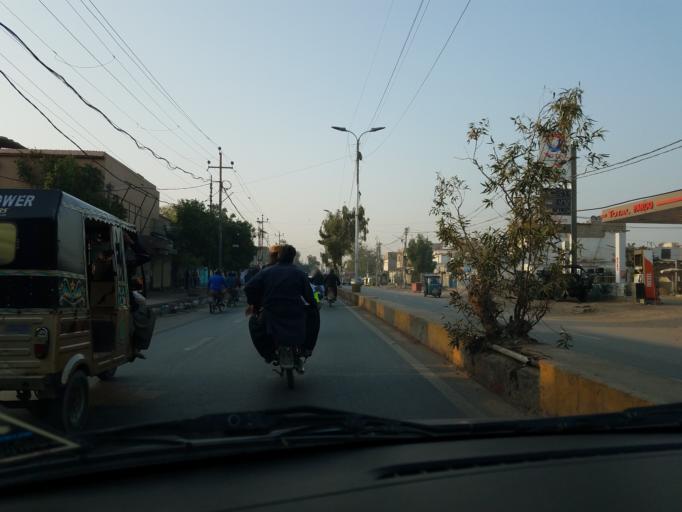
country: PK
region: Sindh
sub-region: Karachi District
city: Karachi
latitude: 24.8896
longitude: 67.0426
